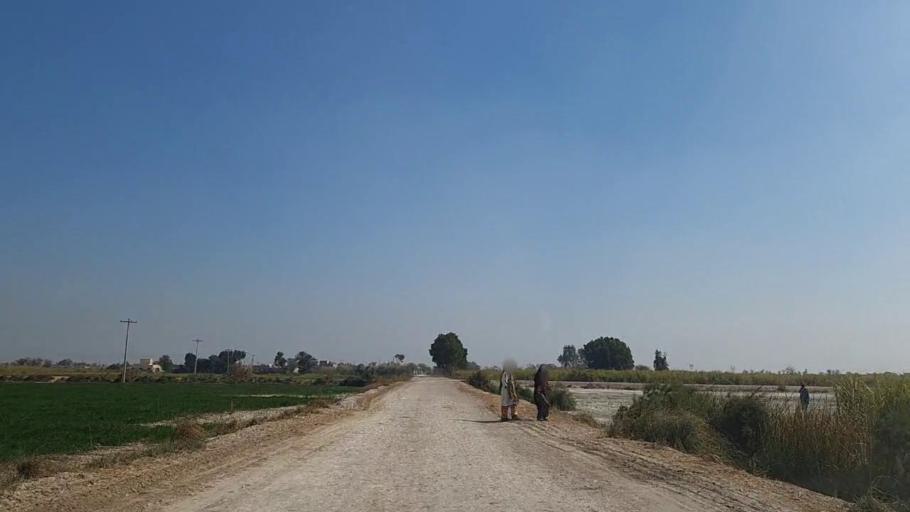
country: PK
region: Sindh
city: Bandhi
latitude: 26.5230
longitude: 68.3148
